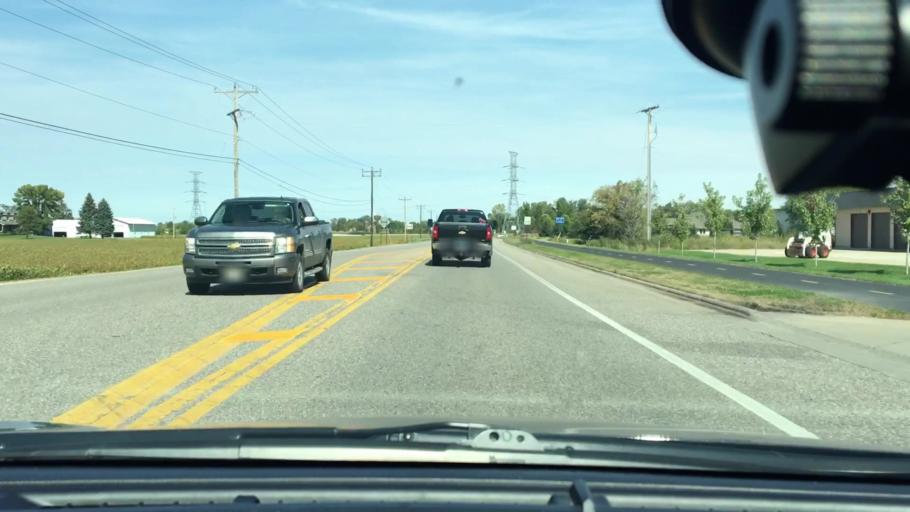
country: US
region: Minnesota
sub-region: Wright County
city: Hanover
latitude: 45.1246
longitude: -93.6358
